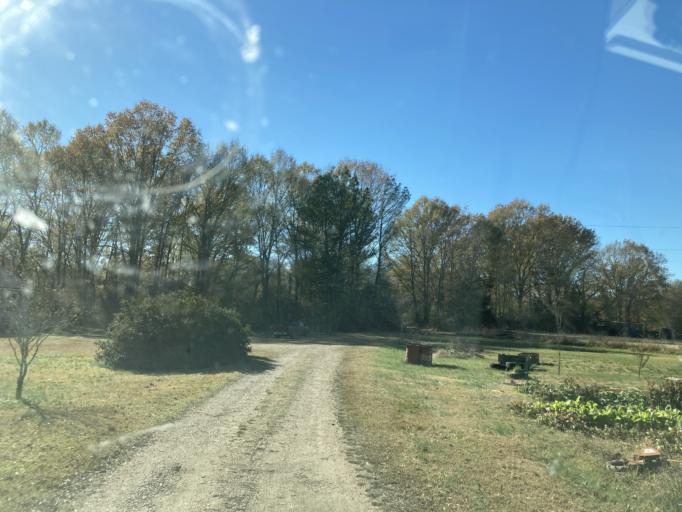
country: US
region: Mississippi
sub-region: Holmes County
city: Pickens
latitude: 32.8562
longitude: -90.0037
